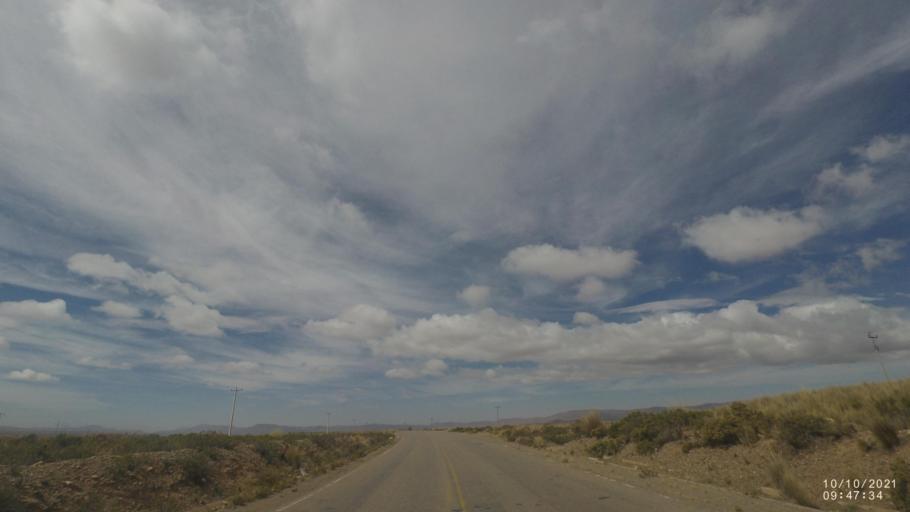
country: BO
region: La Paz
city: Quime
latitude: -17.1959
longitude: -67.3415
